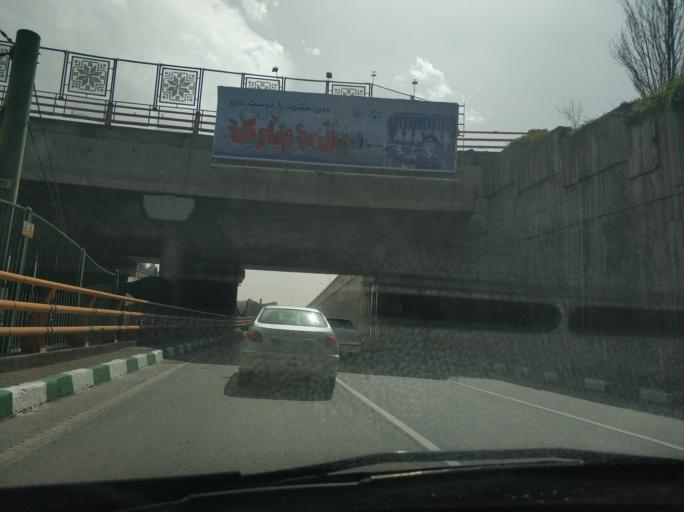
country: IR
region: Razavi Khorasan
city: Mashhad
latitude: 36.3149
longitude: 59.5407
